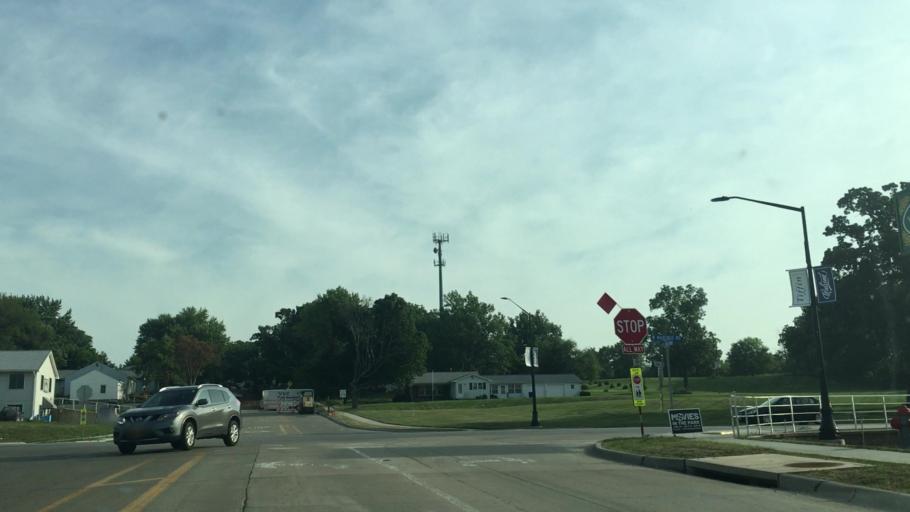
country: US
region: Iowa
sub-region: Johnson County
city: Tiffin
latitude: 41.7069
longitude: -91.6668
